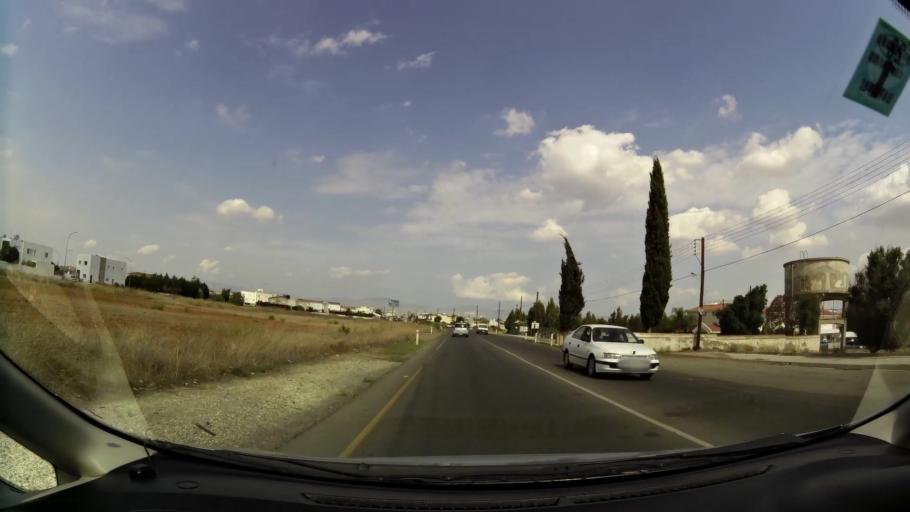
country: CY
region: Lefkosia
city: Tseri
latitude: 35.1106
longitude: 33.3323
